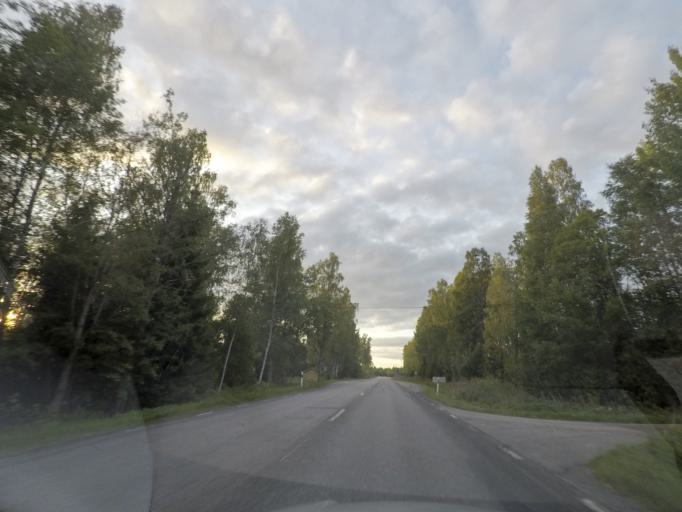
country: SE
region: OErebro
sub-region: Hallefors Kommun
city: Haellefors
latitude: 59.7475
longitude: 14.5107
